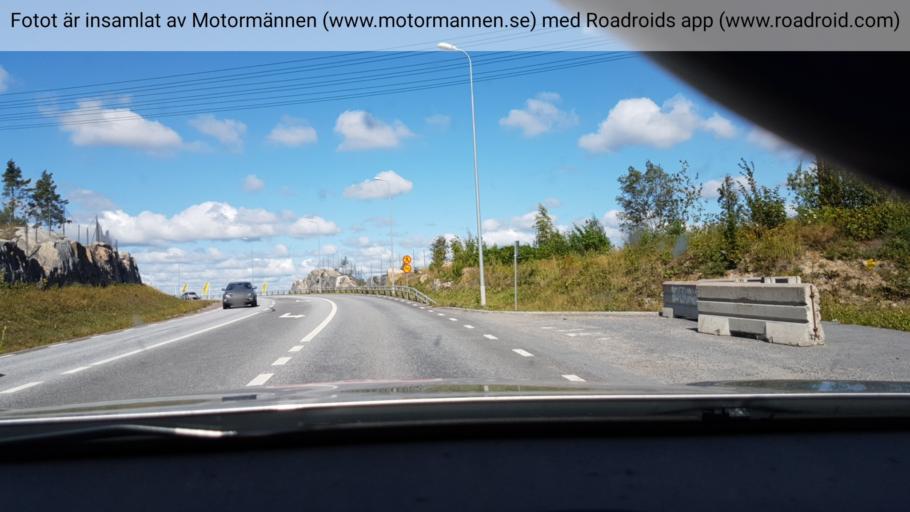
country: SE
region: Stockholm
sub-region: Norrtalje Kommun
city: Norrtalje
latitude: 59.7667
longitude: 18.6895
